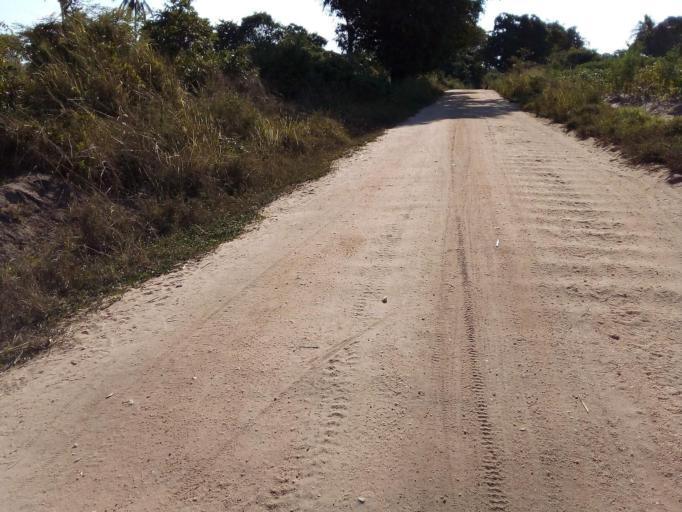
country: MZ
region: Zambezia
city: Quelimane
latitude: -17.5233
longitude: 36.6137
